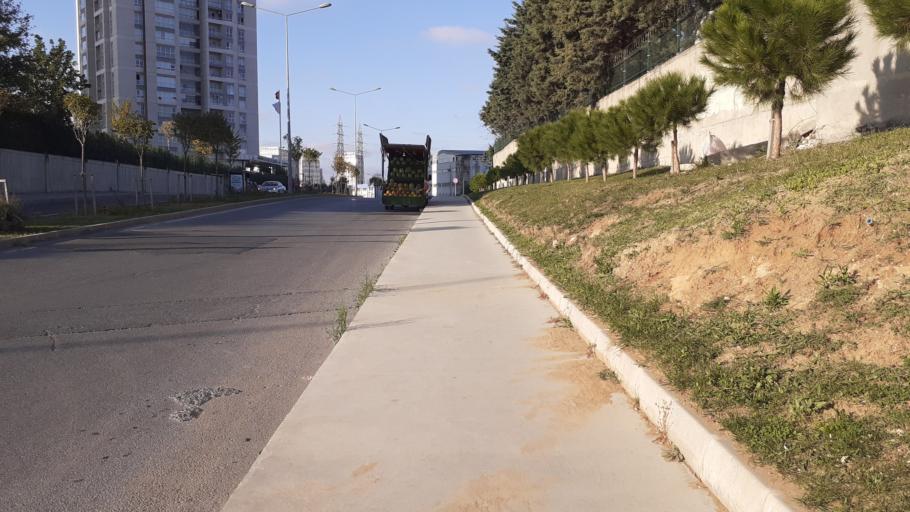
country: TR
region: Istanbul
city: Basaksehir
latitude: 41.0643
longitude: 28.7809
